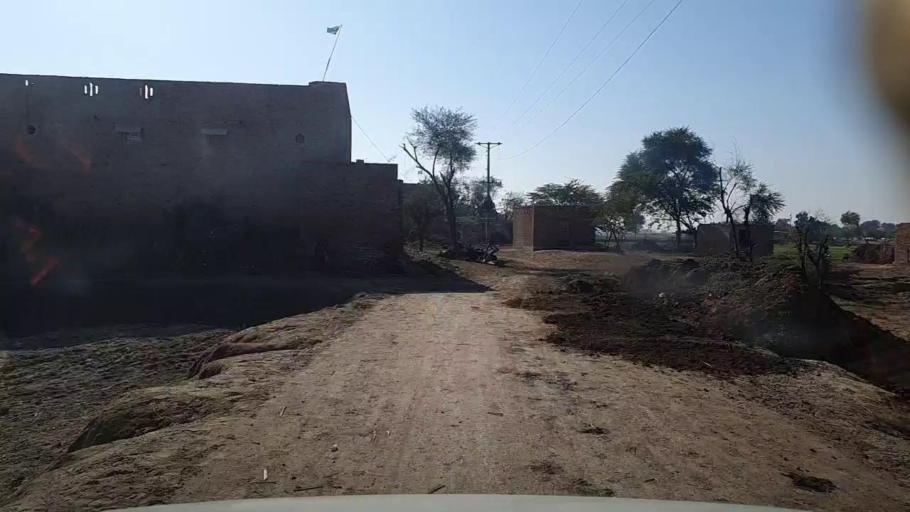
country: PK
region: Sindh
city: Khairpur
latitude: 28.0502
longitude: 69.7329
